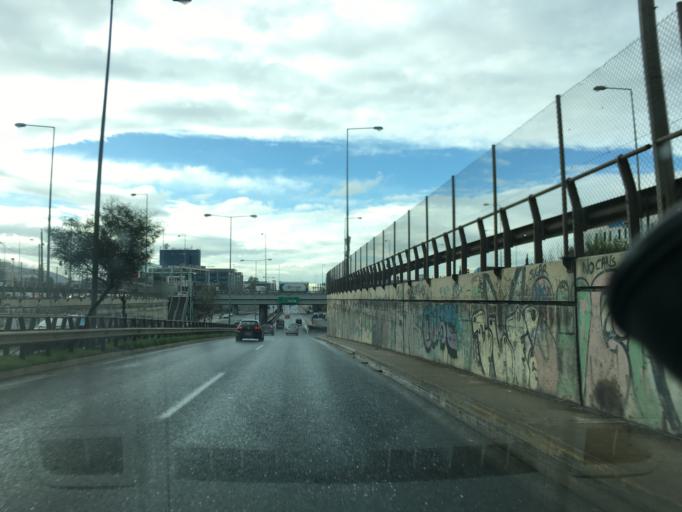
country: GR
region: Attica
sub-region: Nomarchia Athinas
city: Marousi
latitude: 38.0438
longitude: 23.8046
